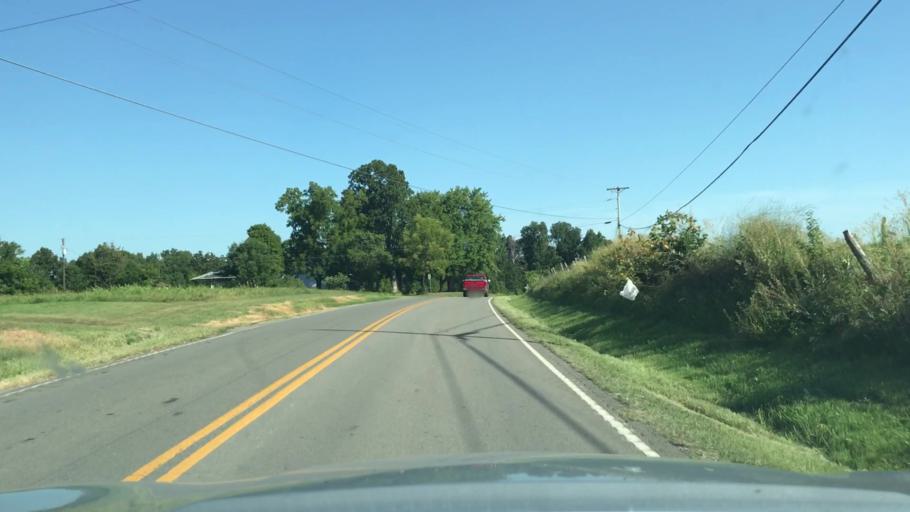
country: US
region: Kentucky
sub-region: Muhlenberg County
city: Greenville
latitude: 37.1717
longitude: -87.1515
